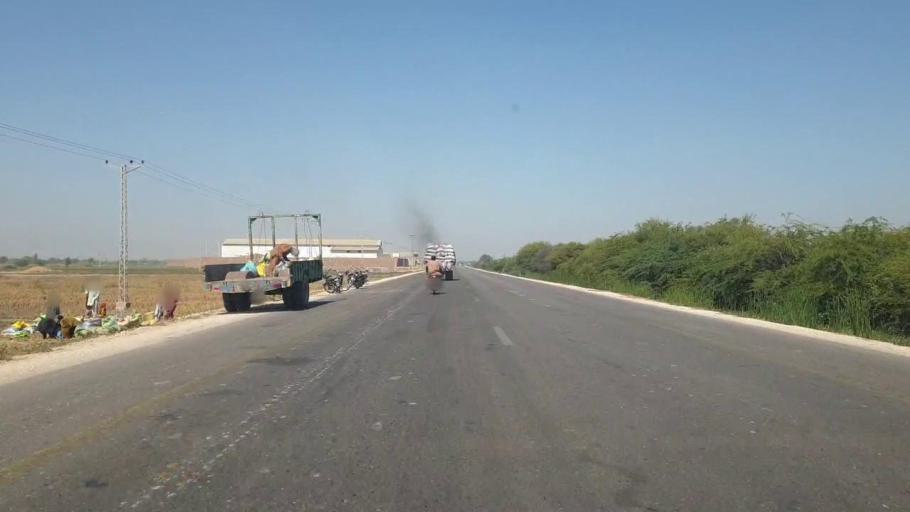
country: PK
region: Sindh
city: Talhar
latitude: 24.8636
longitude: 68.8167
